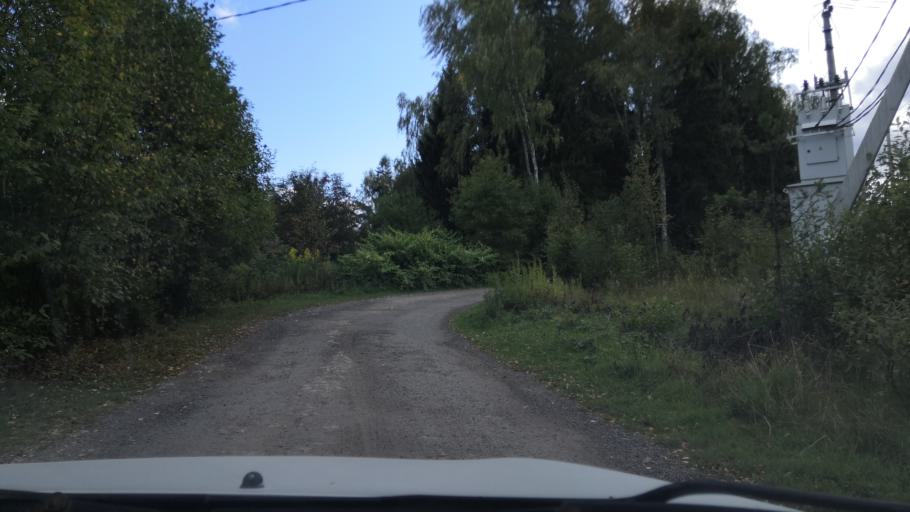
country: RU
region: Moskovskaya
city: Povarovo
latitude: 56.0561
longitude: 37.0206
